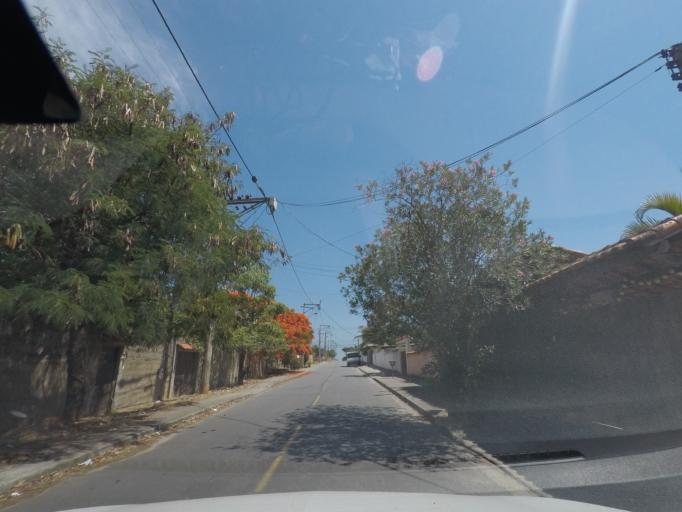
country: BR
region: Rio de Janeiro
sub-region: Marica
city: Marica
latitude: -22.9637
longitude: -42.9594
